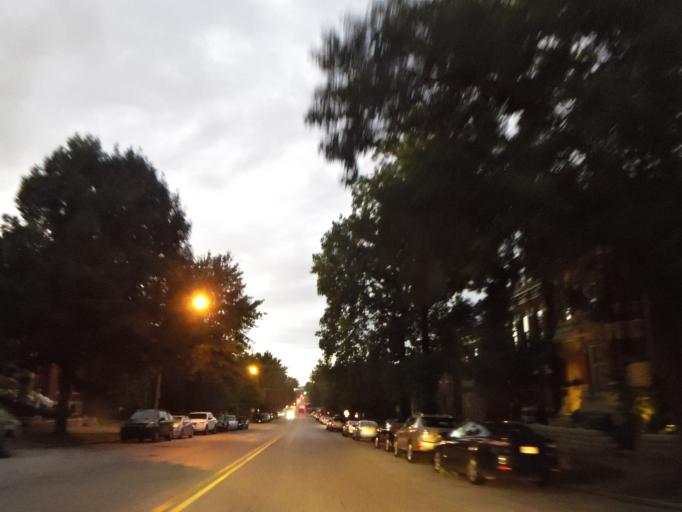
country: US
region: Missouri
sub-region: City of Saint Louis
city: St. Louis
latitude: 38.6050
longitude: -90.2109
